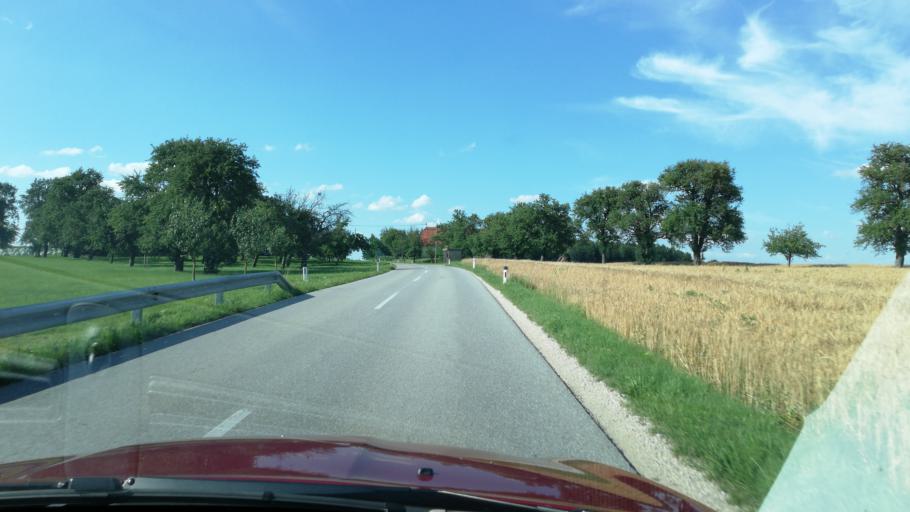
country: AT
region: Upper Austria
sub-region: Politischer Bezirk Steyr-Land
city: Pfarrkirchen bei Bad Hall
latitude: 48.0048
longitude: 14.2220
